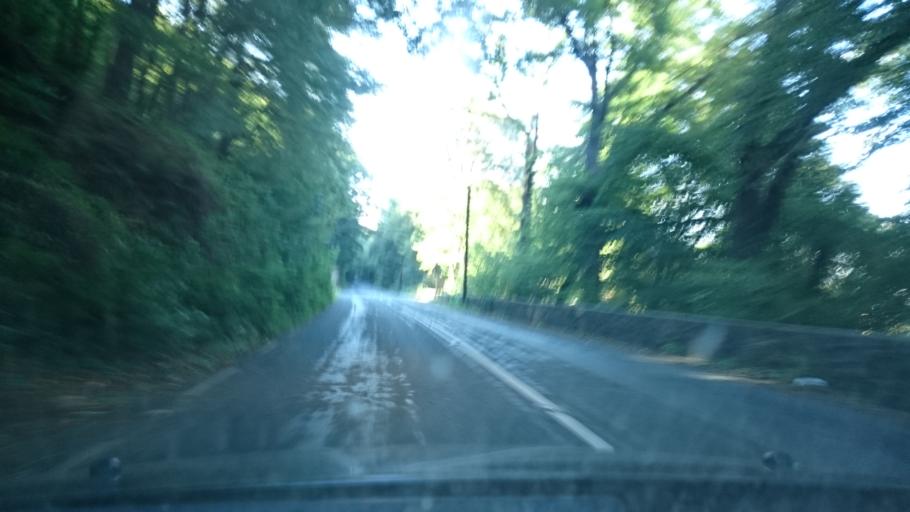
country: IE
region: Leinster
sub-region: Kilkenny
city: Graiguenamanagh
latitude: 52.5296
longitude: -6.9541
